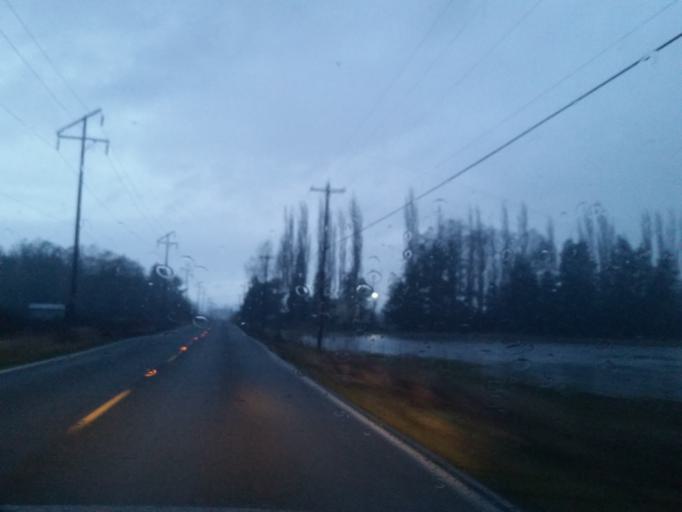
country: US
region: Washington
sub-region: Snohomish County
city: Everett
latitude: 47.9659
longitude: -122.1737
